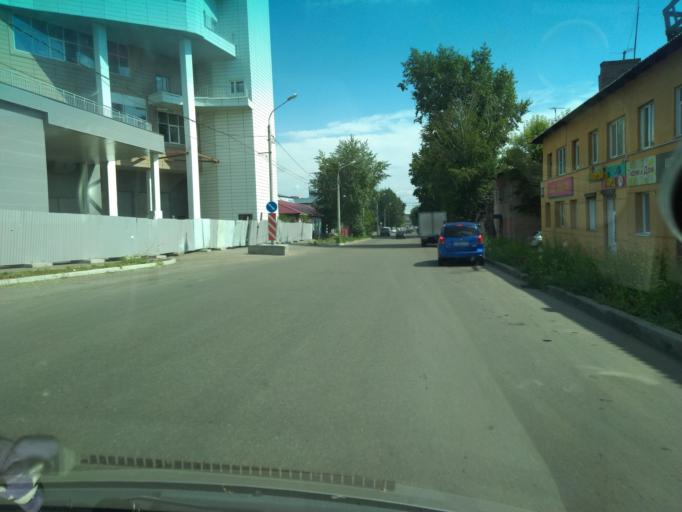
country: RU
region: Krasnoyarskiy
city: Krasnoyarsk
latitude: 56.0284
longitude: 92.8893
